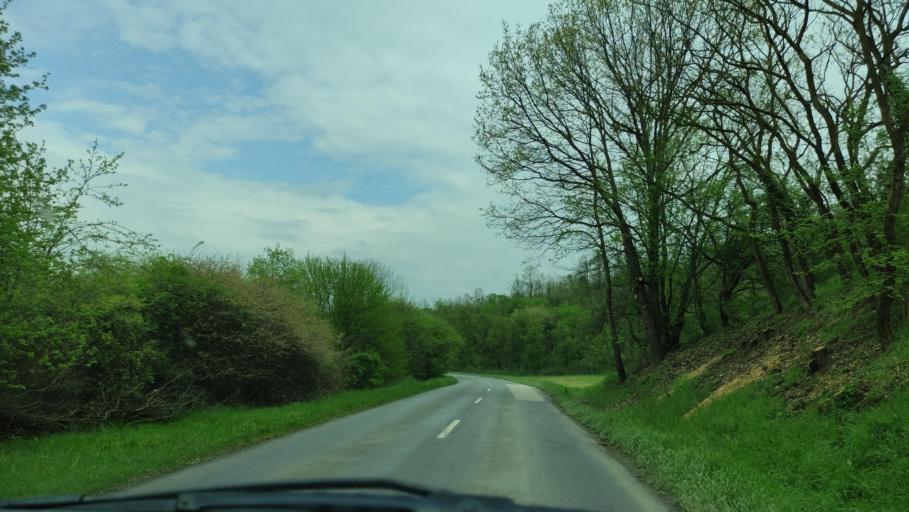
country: HU
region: Baranya
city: Komlo
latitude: 46.2228
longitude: 18.2395
